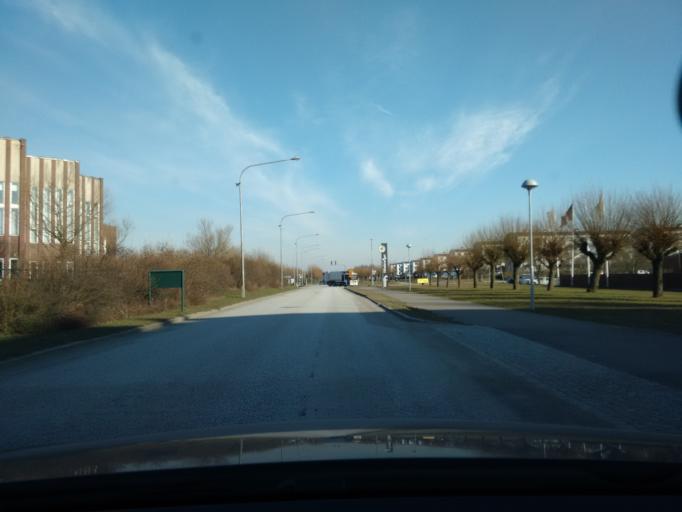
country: SE
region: Skane
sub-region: Lunds Kommun
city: Lund
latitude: 55.7232
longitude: 13.2022
